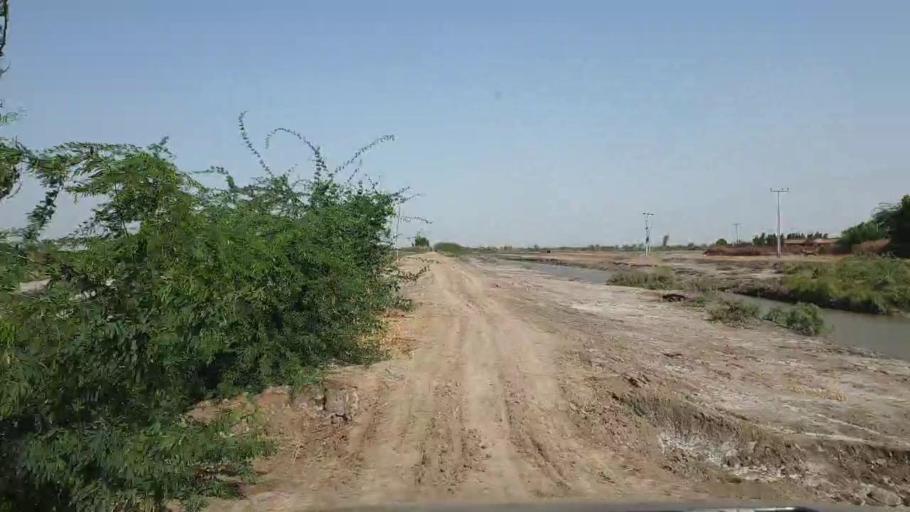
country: PK
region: Sindh
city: Tando Bago
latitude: 24.7003
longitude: 69.0706
